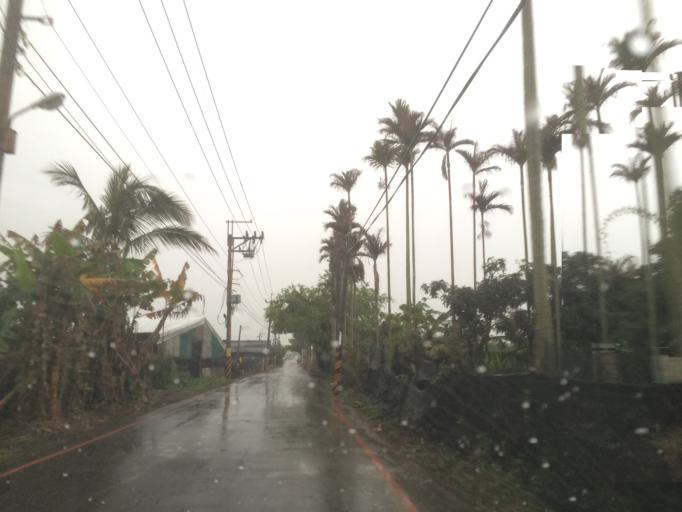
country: TW
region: Taiwan
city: Fengyuan
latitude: 24.2093
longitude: 120.8032
